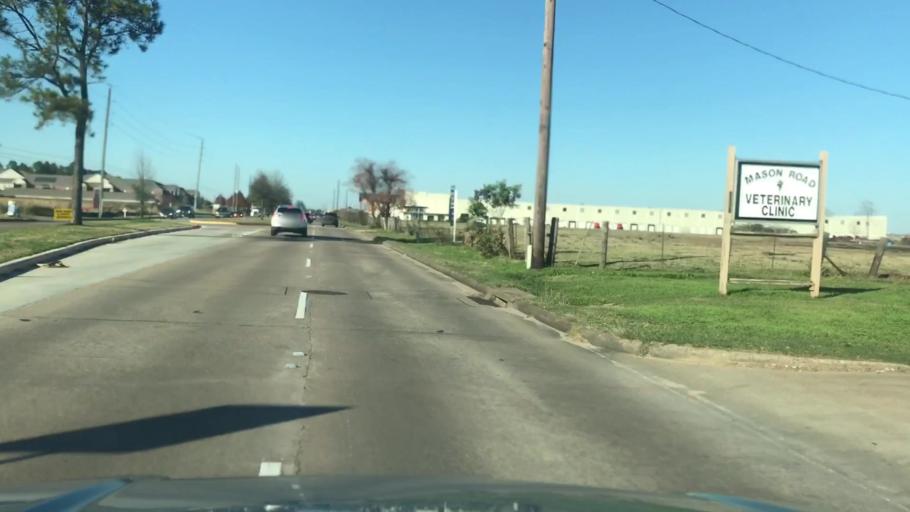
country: US
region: Texas
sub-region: Fort Bend County
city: Cinco Ranch
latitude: 29.8028
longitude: -95.7519
